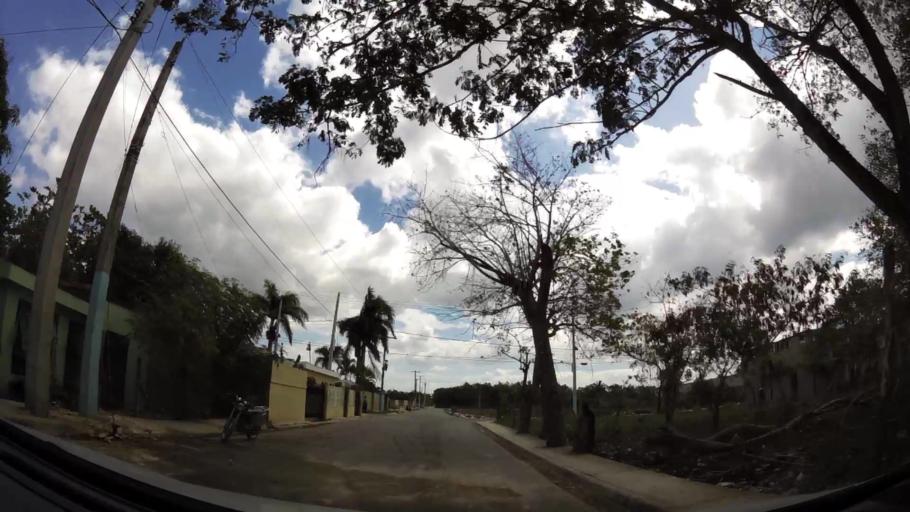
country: DO
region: Santo Domingo
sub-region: Santo Domingo
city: Boca Chica
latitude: 18.4530
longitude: -69.6424
